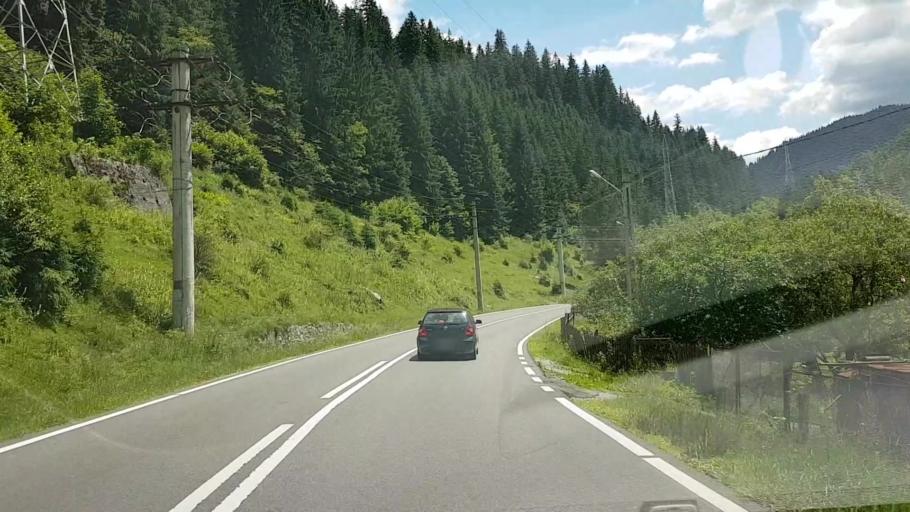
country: RO
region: Suceava
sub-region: Comuna Brosteni
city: Brosteni
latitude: 47.2692
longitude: 25.6543
